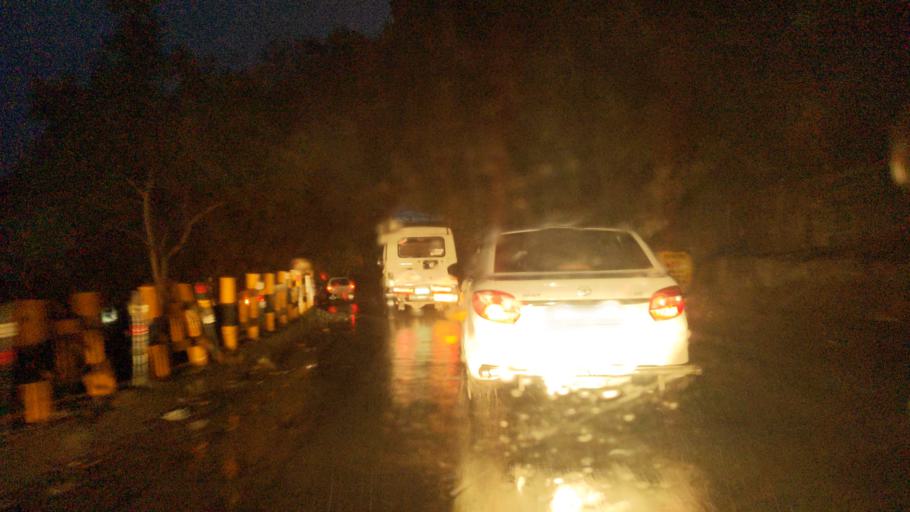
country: IN
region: Uttarakhand
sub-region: Naini Tal
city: Haldwani
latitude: 29.2797
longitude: 79.5450
